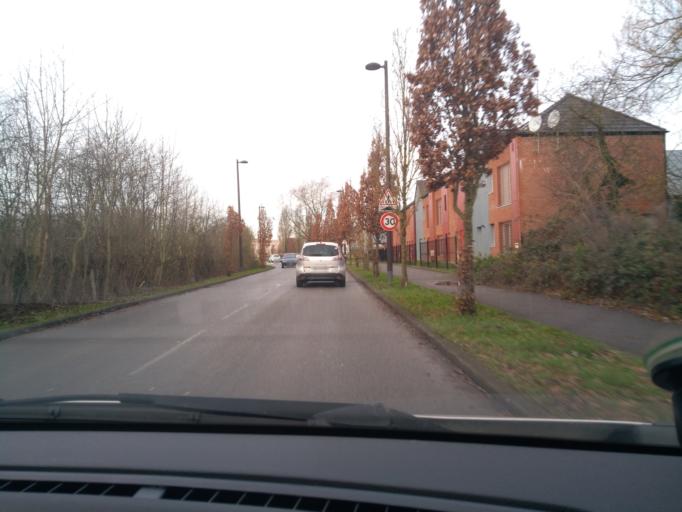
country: FR
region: Nord-Pas-de-Calais
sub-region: Departement du Nord
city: Maubeuge
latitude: 50.2893
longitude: 3.9736
